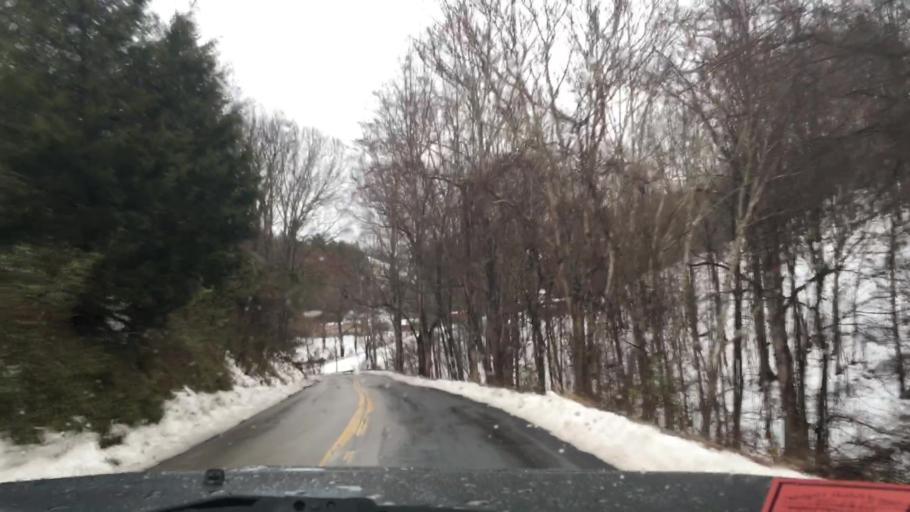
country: US
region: Virginia
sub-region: Pulaski County
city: Dublin
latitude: 37.0058
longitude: -80.6660
